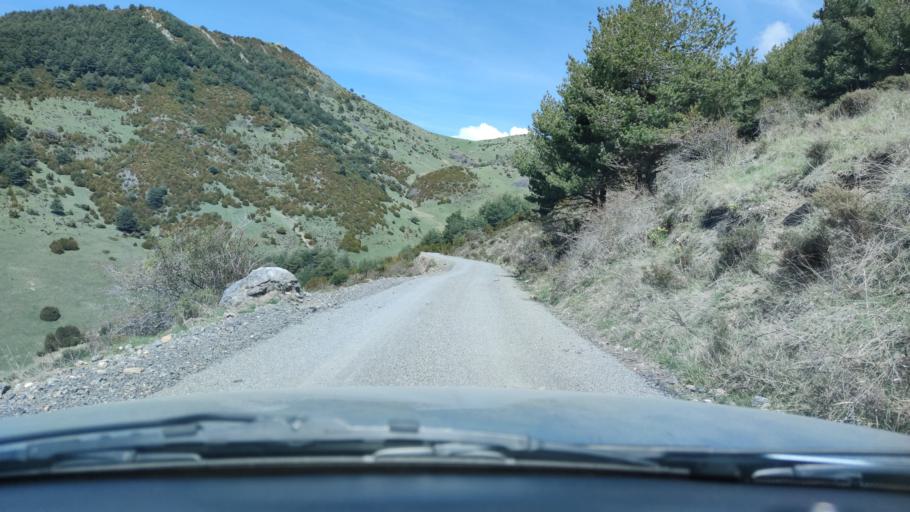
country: ES
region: Catalonia
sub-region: Provincia de Lleida
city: Sort
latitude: 42.3106
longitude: 1.1657
